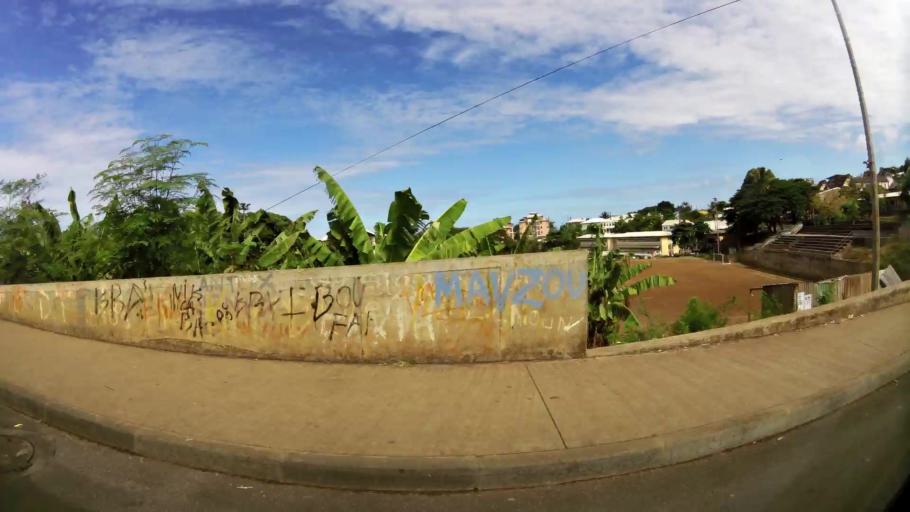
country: YT
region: Mamoudzou
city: Mamoudzou
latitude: -12.7809
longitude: 45.2281
